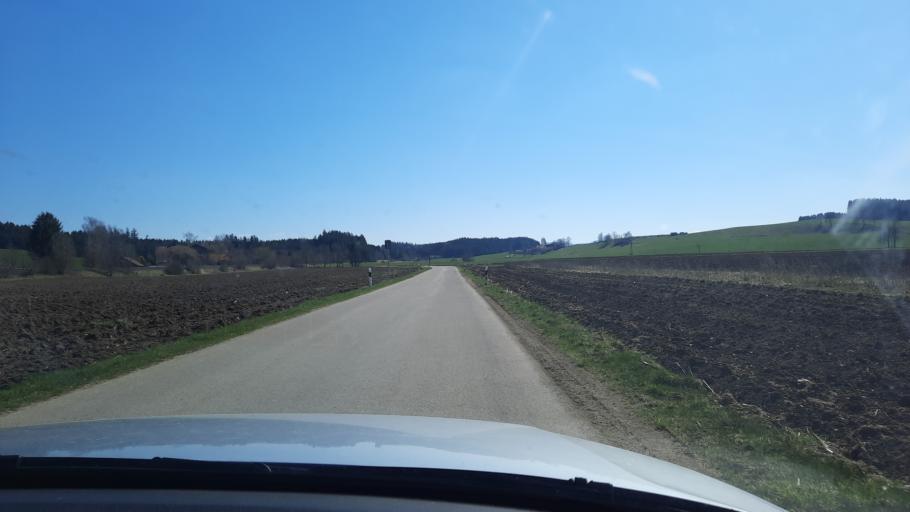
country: DE
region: Bavaria
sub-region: Swabia
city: Wolfertschwenden
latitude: 47.8532
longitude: 10.2543
